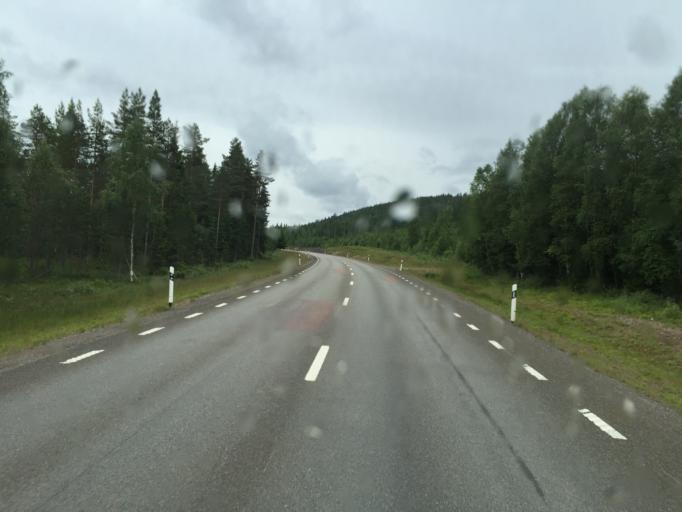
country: SE
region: Dalarna
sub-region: Malung-Saelens kommun
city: Malung
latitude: 60.6385
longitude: 13.6180
